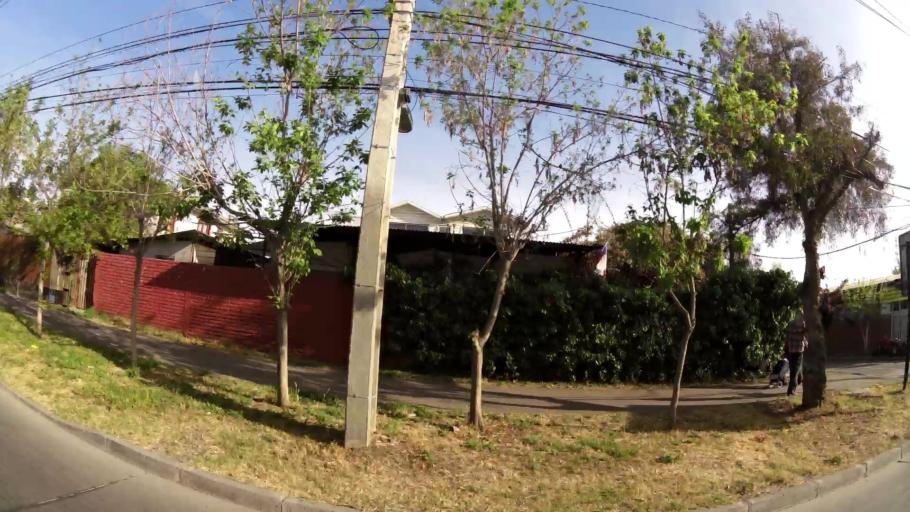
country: CL
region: Santiago Metropolitan
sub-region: Provincia de Santiago
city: La Pintana
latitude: -33.5436
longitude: -70.5836
